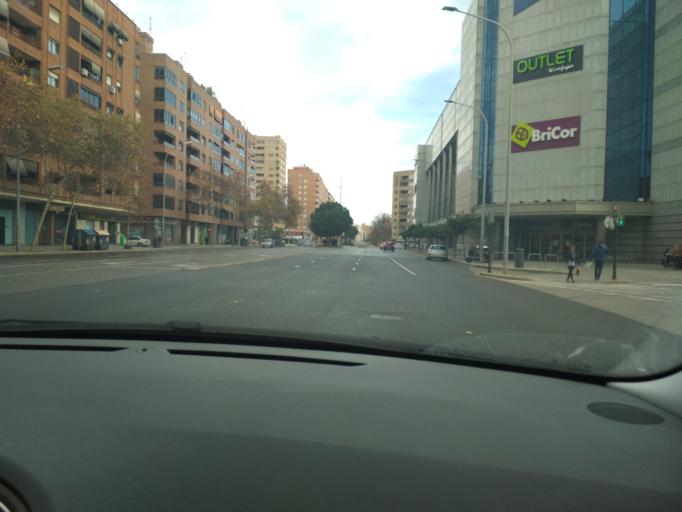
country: ES
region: Valencia
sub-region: Provincia de Valencia
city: Mislata
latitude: 39.4849
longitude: -0.3980
